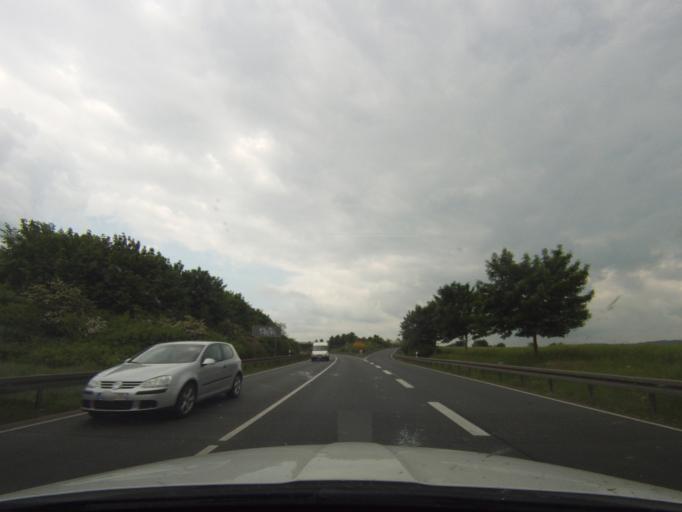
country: DE
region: Thuringia
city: Saalfeld
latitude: 50.6642
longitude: 11.3483
